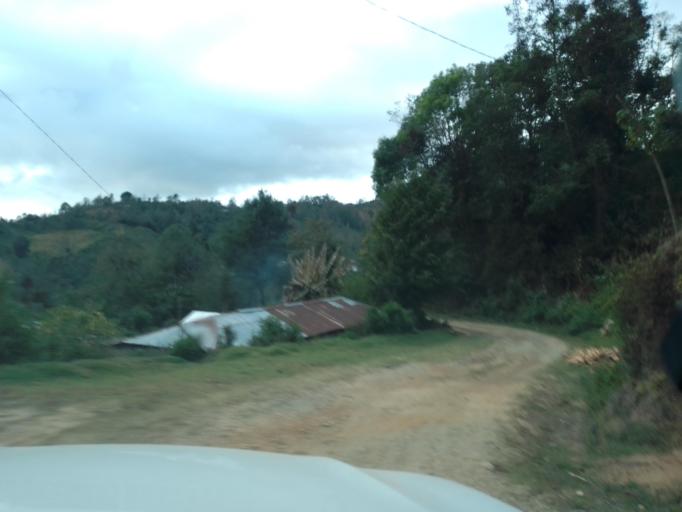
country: MX
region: Chiapas
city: Motozintla de Mendoza
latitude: 15.2166
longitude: -92.2308
